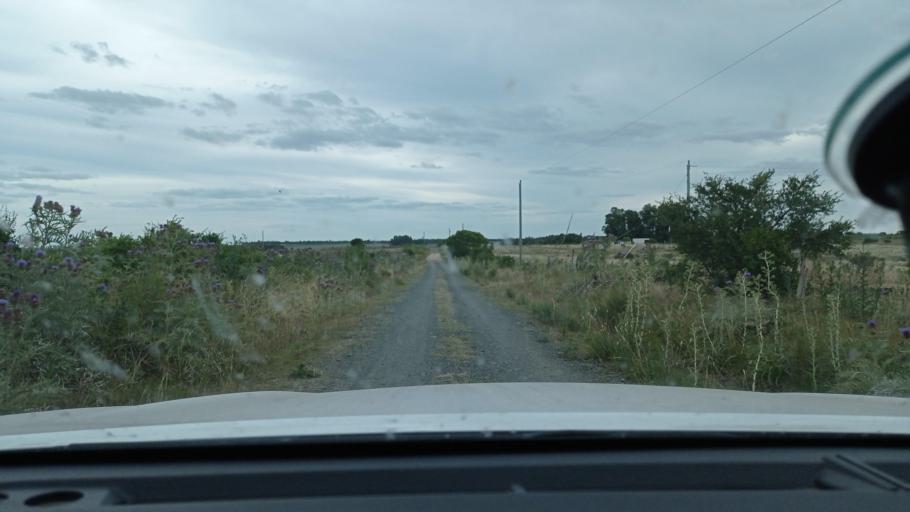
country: UY
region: Florida
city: Casupa
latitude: -34.1478
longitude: -55.7962
